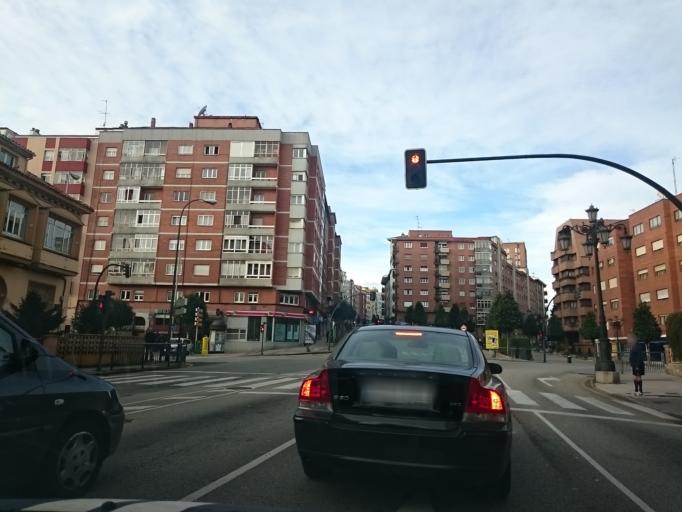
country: ES
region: Asturias
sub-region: Province of Asturias
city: Oviedo
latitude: 43.3566
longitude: -5.8629
